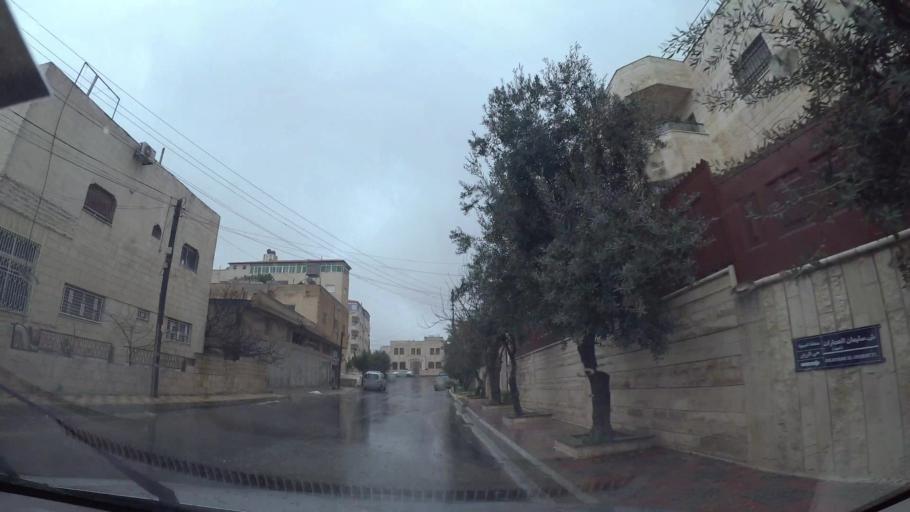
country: JO
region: Amman
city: Al Jubayhah
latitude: 32.0354
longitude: 35.8822
